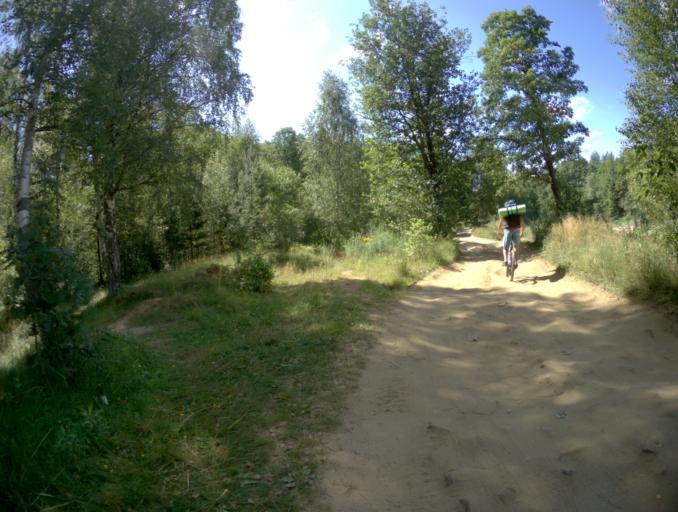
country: RU
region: Nizjnij Novgorod
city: Sitniki
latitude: 56.4595
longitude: 44.0178
